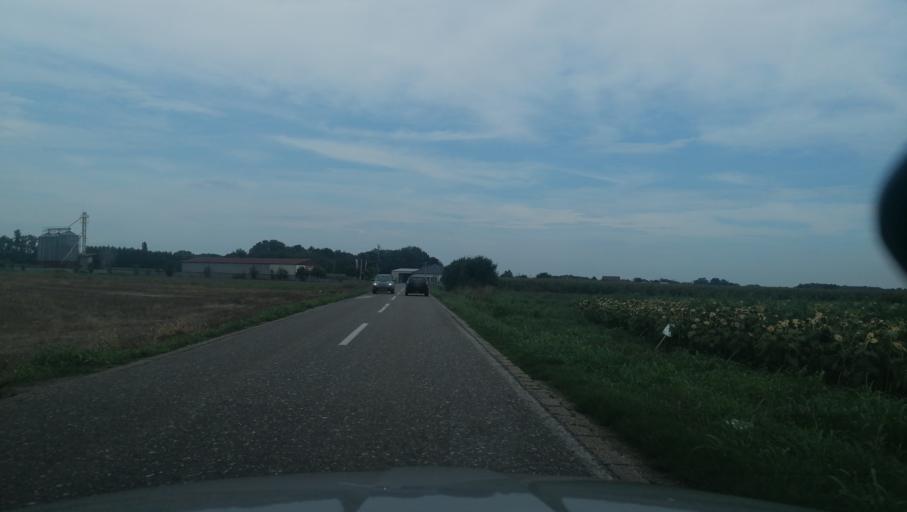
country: RS
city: Klenje
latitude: 44.8227
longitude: 19.4535
